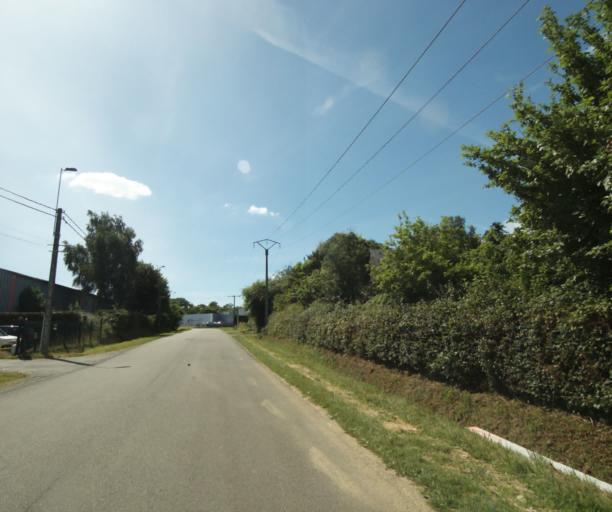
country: FR
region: Pays de la Loire
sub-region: Departement de la Mayenne
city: Change
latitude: 48.0742
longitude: -0.7978
